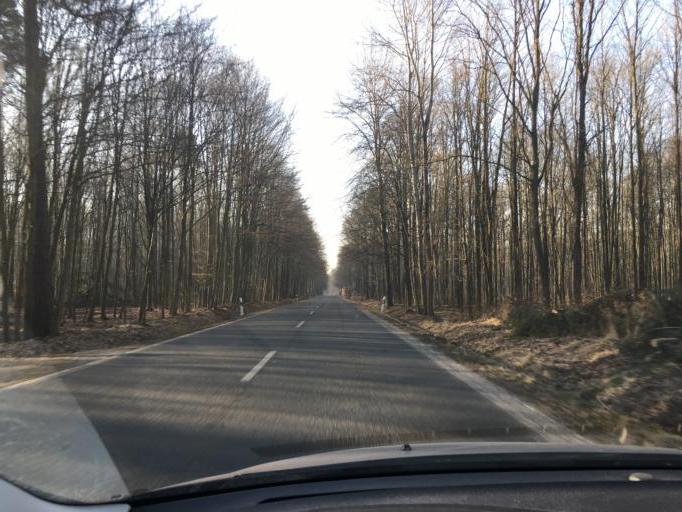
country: DE
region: Thuringia
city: Langenleuba-Niederhain
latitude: 50.9865
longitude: 12.5634
